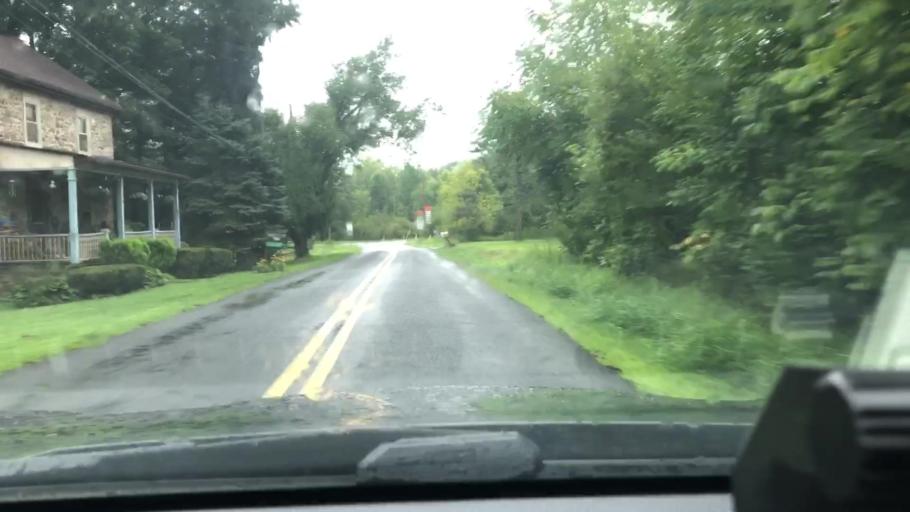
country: US
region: Pennsylvania
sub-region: Lehigh County
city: Macungie
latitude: 40.4668
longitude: -75.5488
